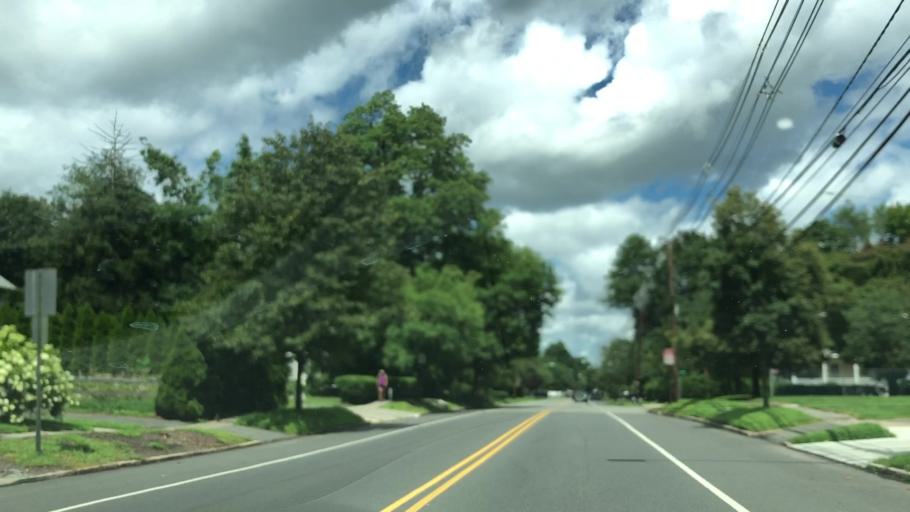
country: US
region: New Jersey
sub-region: Essex County
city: Glen Ridge
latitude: 40.8055
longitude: -74.2173
